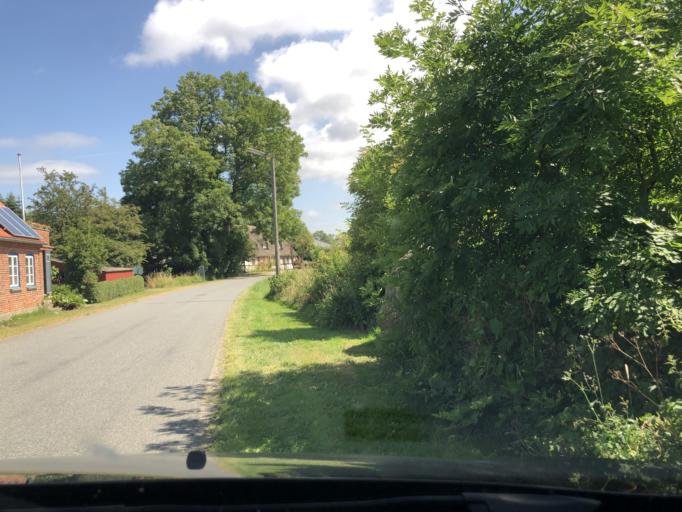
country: DK
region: South Denmark
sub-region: AEro Kommune
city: AEroskobing
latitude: 54.9147
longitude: 10.2961
